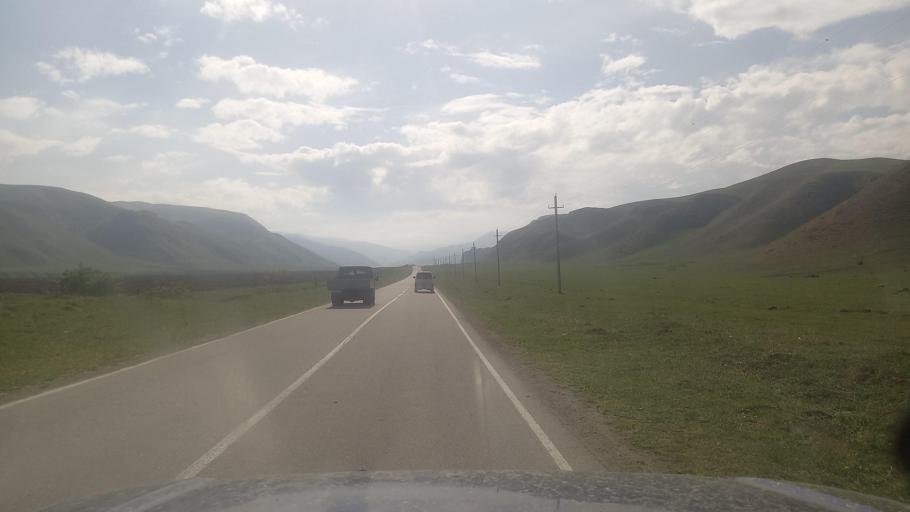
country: RU
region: Kabardino-Balkariya
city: Kamennomostskoye
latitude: 43.7357
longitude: 42.9880
